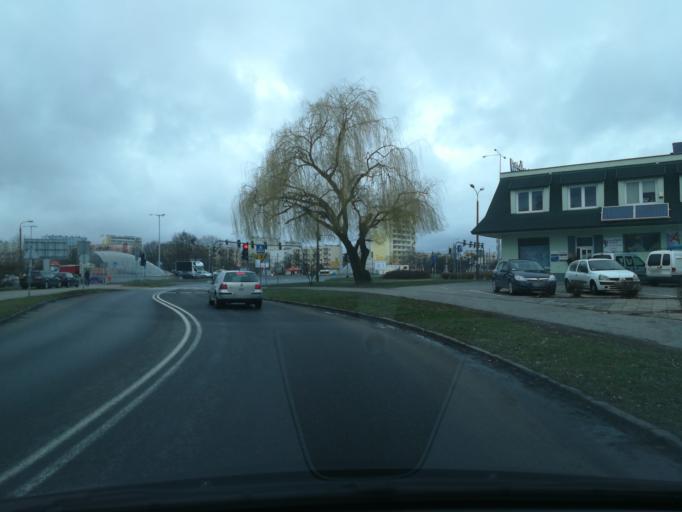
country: PL
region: Kujawsko-Pomorskie
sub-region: Powiat torunski
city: Lubicz Dolny
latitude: 53.0261
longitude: 18.6816
